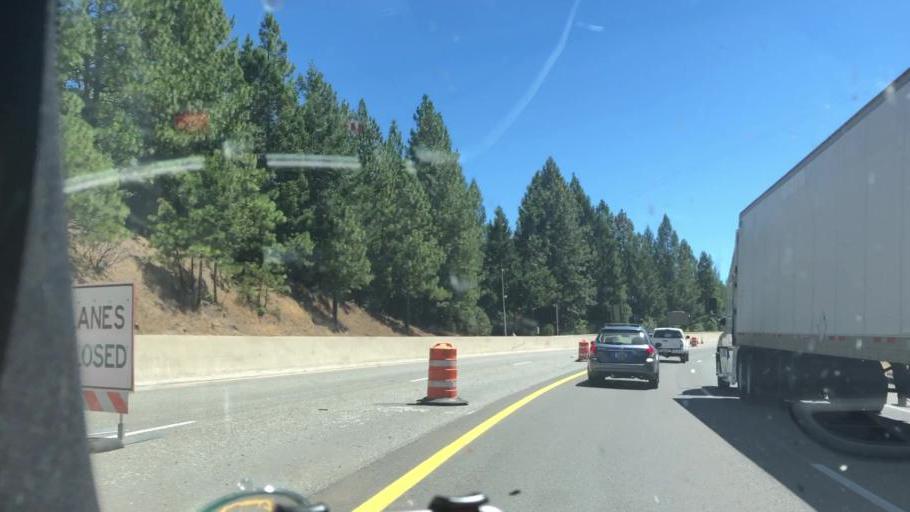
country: US
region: California
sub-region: Placer County
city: Colfax
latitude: 39.1393
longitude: -120.9275
